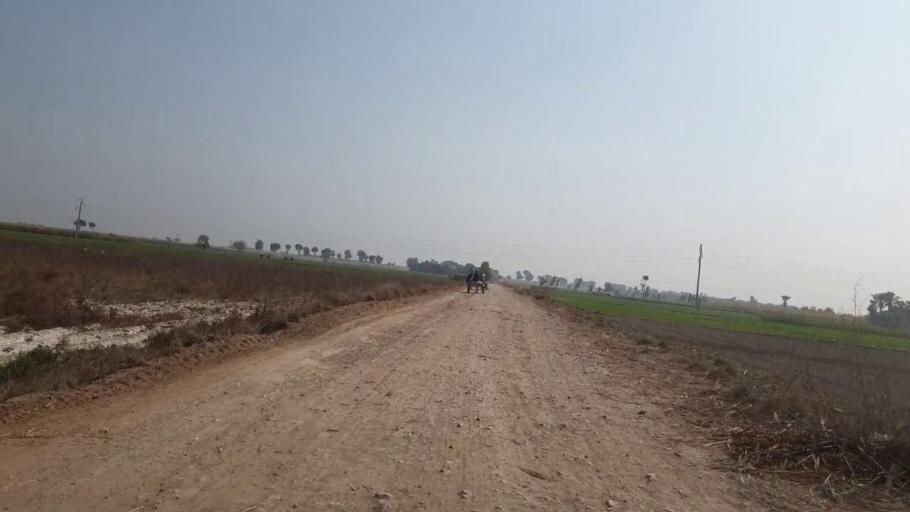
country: PK
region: Sindh
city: Bhit Shah
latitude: 25.7180
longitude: 68.5442
